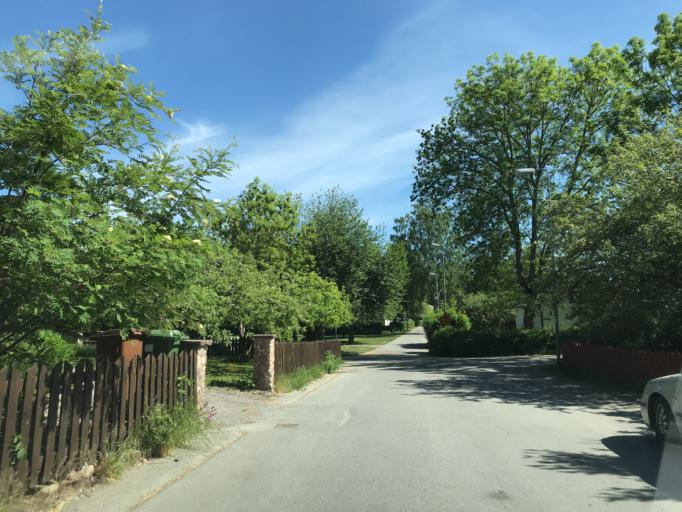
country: SE
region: Stockholm
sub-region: Sollentuna Kommun
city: Sollentuna
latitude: 59.4267
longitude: 17.9609
